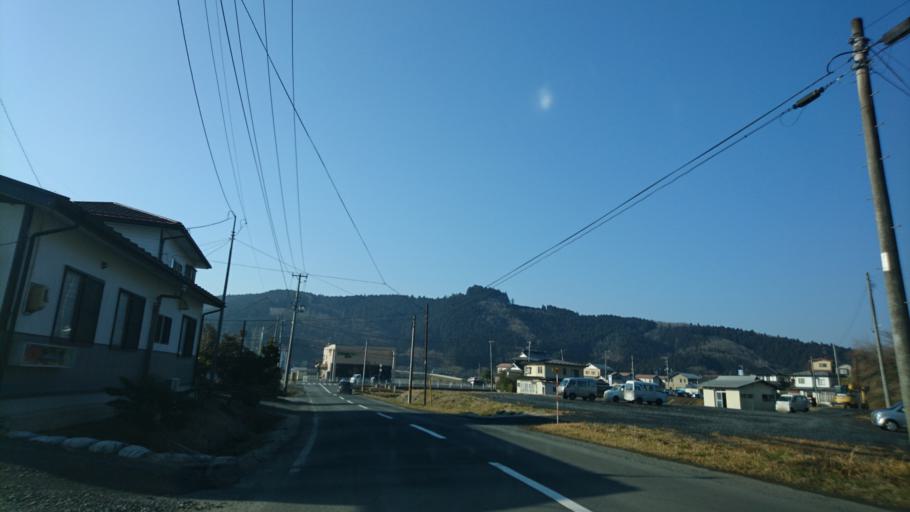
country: JP
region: Iwate
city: Ichinoseki
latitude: 38.9008
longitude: 141.2793
